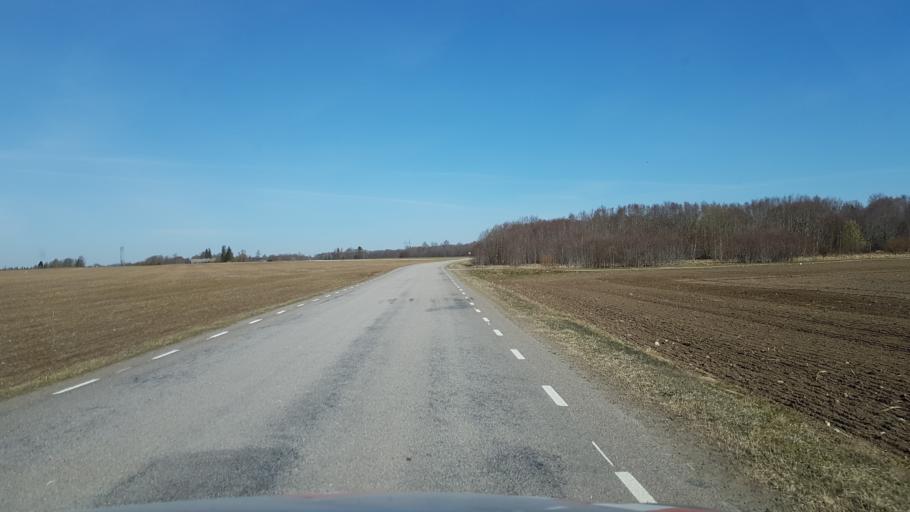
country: EE
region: Laeaene-Virumaa
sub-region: Vinni vald
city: Vinni
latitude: 59.2328
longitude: 26.3423
